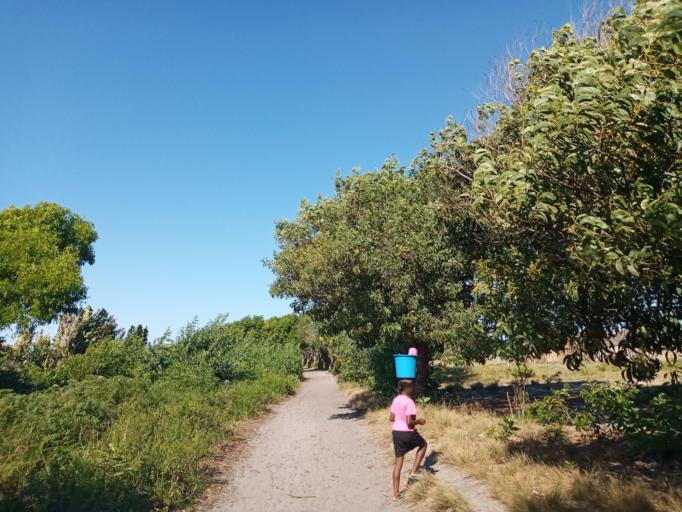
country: MG
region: Anosy
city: Fort Dauphin
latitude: -24.9061
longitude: 47.1021
